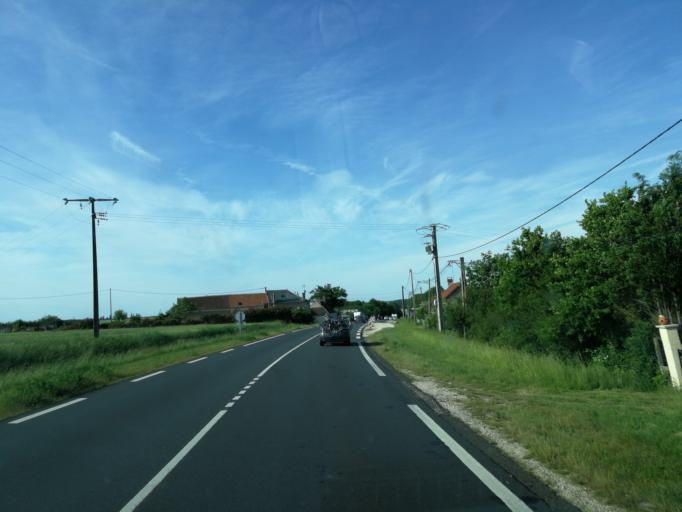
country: FR
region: Centre
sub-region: Departement du Loir-et-Cher
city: Moree
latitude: 47.9261
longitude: 1.1939
